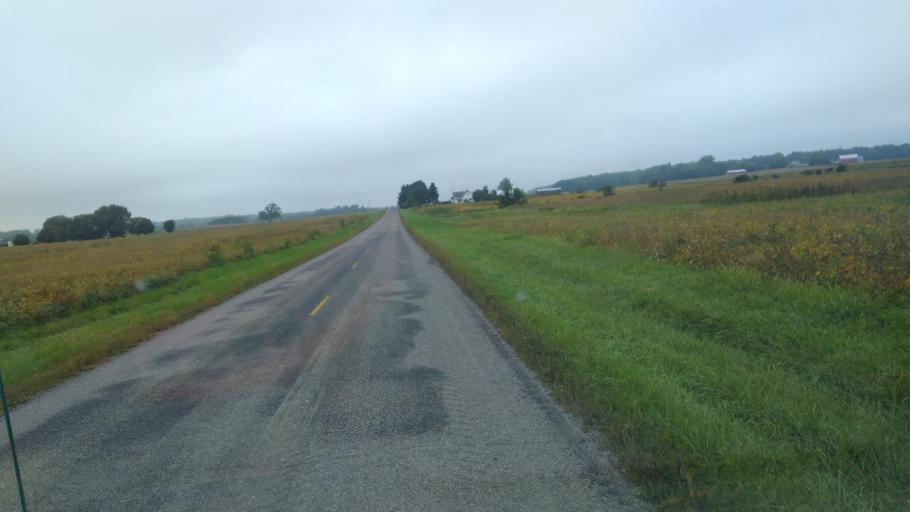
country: US
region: Ohio
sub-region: Hardin County
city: Kenton
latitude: 40.5449
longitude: -83.6343
